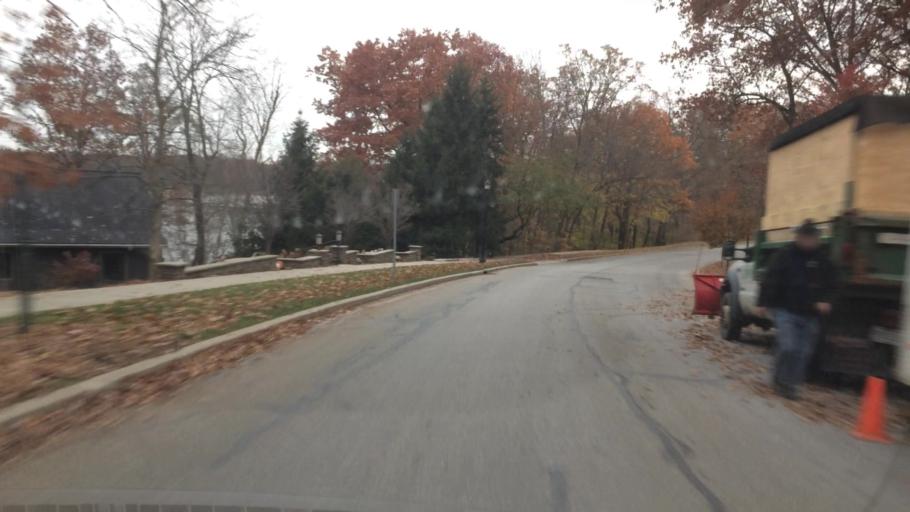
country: US
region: Ohio
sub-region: Summit County
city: Silver Lake
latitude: 41.1624
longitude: -81.4613
